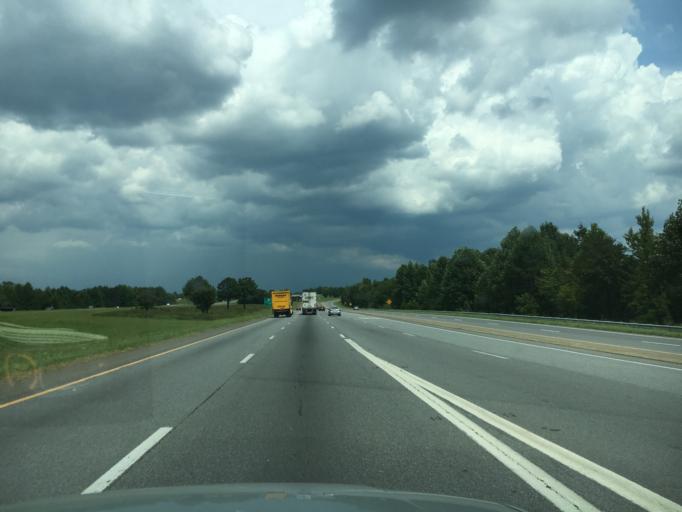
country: US
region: North Carolina
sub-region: Cleveland County
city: Kings Mountain
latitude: 35.2453
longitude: -81.3051
